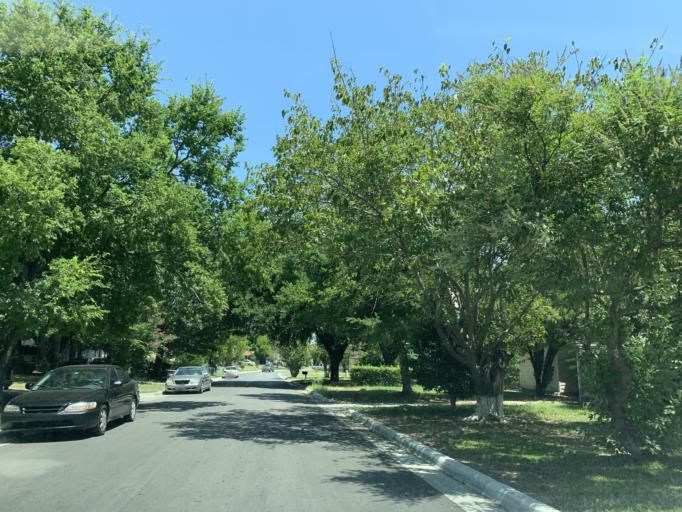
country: US
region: Texas
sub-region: Dallas County
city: Hutchins
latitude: 32.6765
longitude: -96.7616
